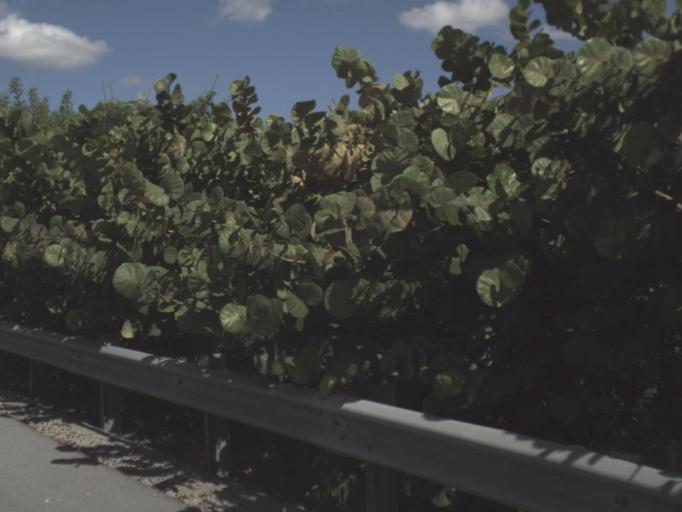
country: US
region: Florida
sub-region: Miami-Dade County
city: Cutler Ridge
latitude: 25.5802
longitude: -80.3652
